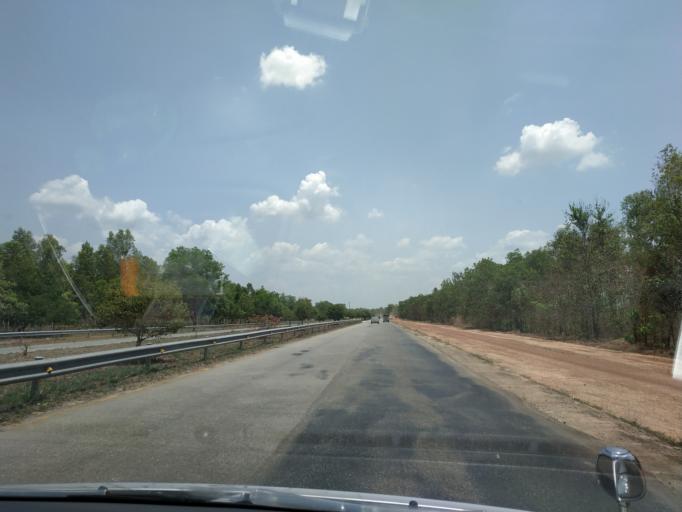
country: MM
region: Bago
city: Thanatpin
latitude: 17.1902
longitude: 96.1922
